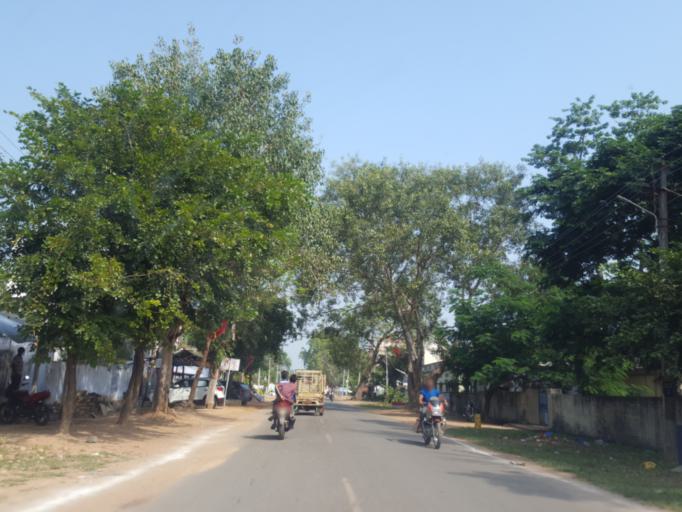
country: IN
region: Telangana
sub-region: Khammam
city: Yellandu
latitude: 17.5978
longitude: 80.3175
